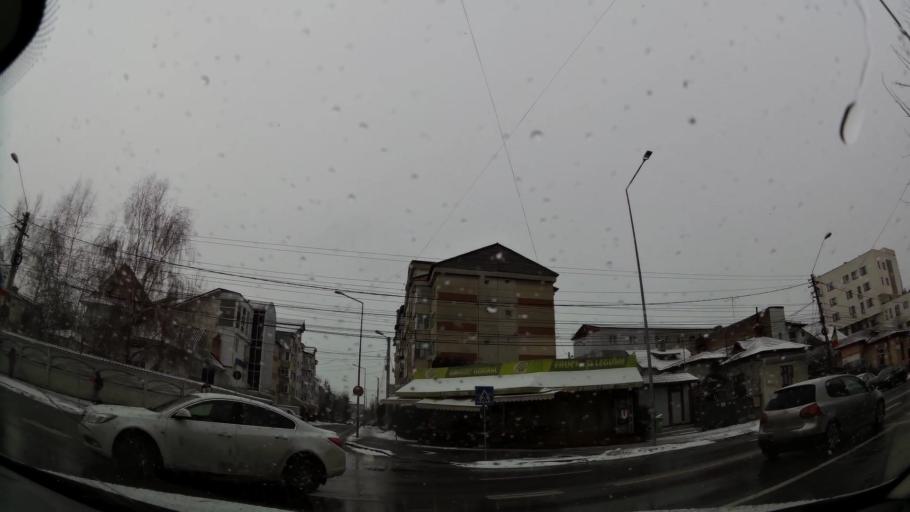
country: RO
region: Dambovita
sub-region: Municipiul Targoviste
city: Targoviste
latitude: 44.9247
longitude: 25.4501
